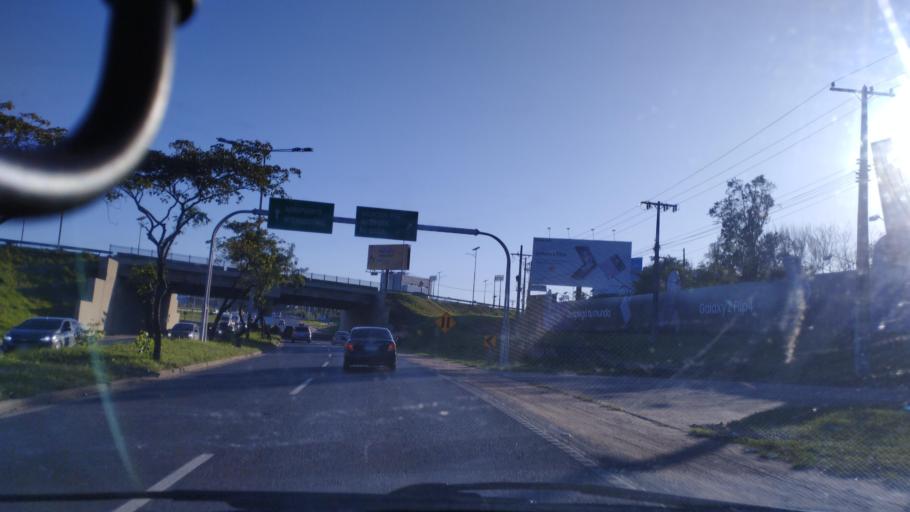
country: PY
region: Central
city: Fernando de la Mora
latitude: -25.2630
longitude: -57.5199
